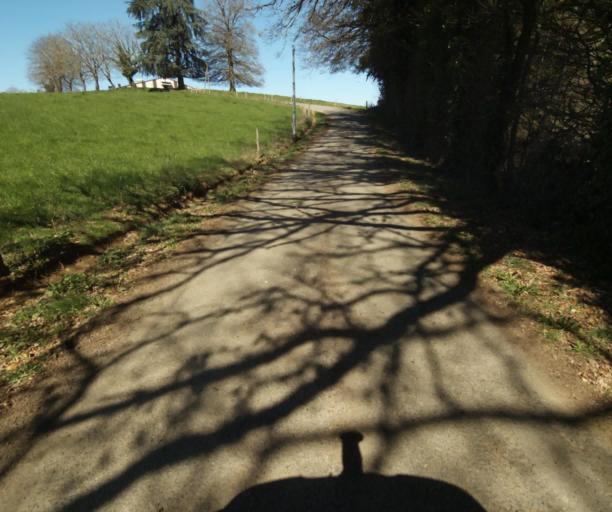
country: FR
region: Limousin
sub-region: Departement de la Correze
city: Uzerche
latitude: 45.4023
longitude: 1.6339
